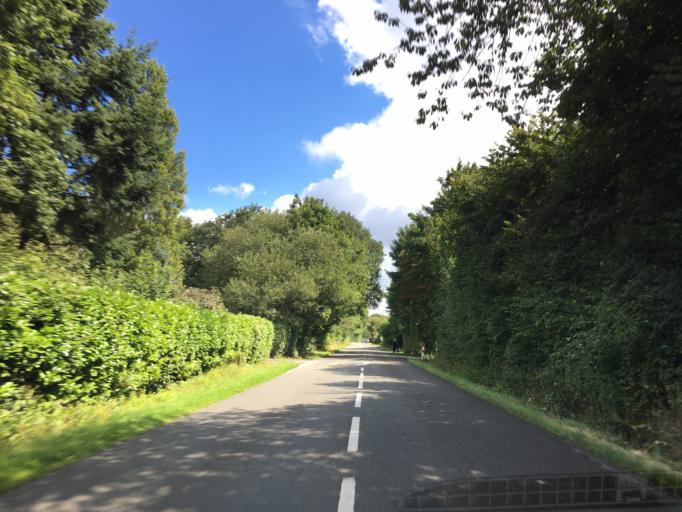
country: FR
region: Lower Normandy
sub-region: Departement du Calvados
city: Houlgate
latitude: 49.2769
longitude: -0.0663
